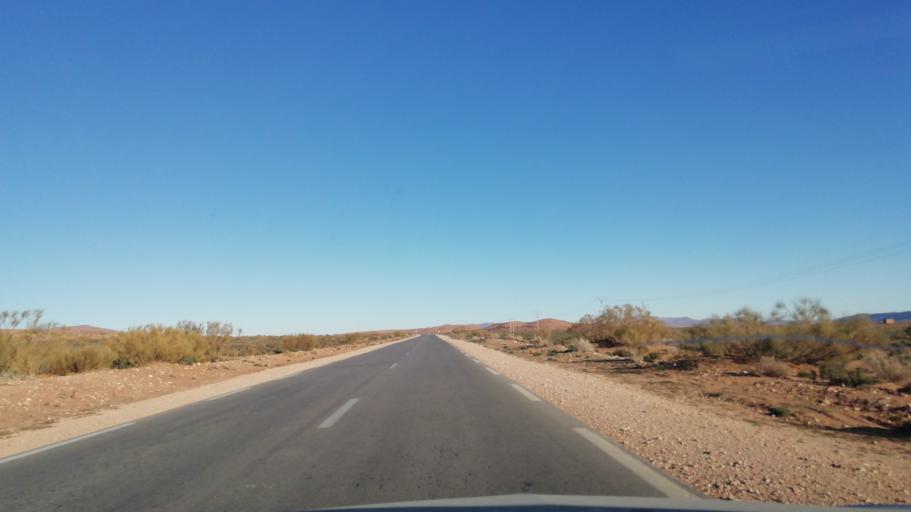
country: DZ
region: El Bayadh
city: El Abiodh Sidi Cheikh
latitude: 33.1610
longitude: 0.3949
